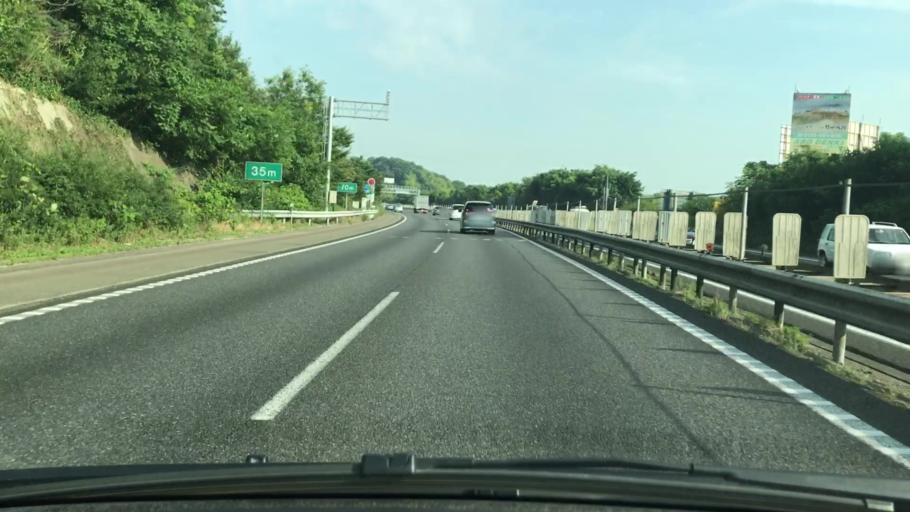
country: JP
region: Hyogo
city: Akashi
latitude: 34.6971
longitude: 134.9675
